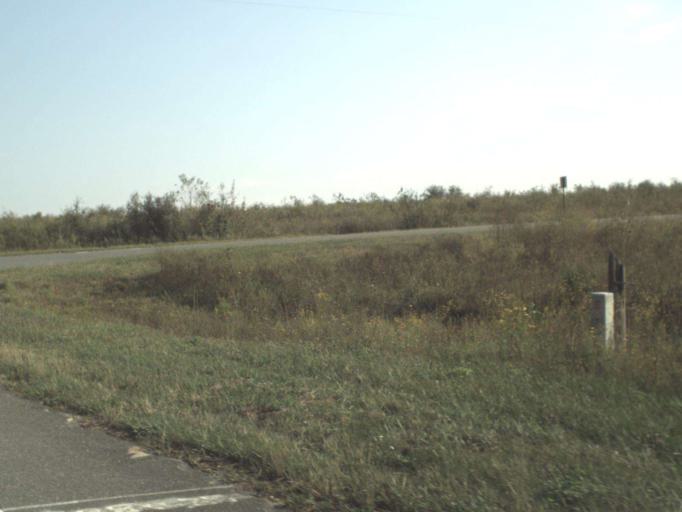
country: US
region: Florida
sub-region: Holmes County
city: Bonifay
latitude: 30.7335
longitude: -85.6853
